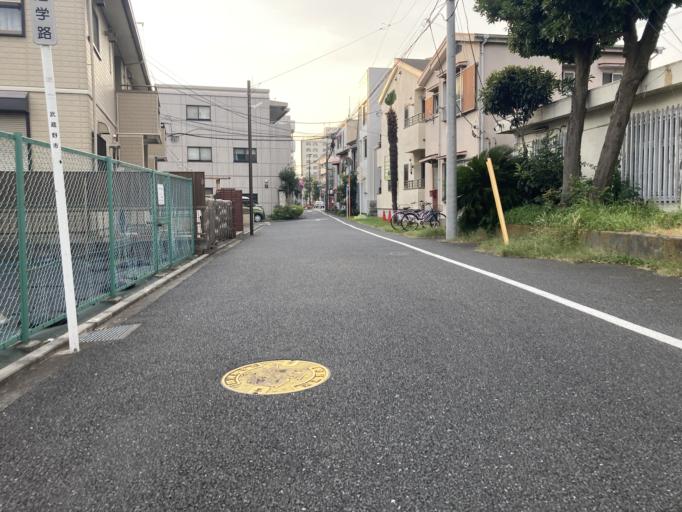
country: JP
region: Tokyo
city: Musashino
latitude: 35.6984
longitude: 139.5894
